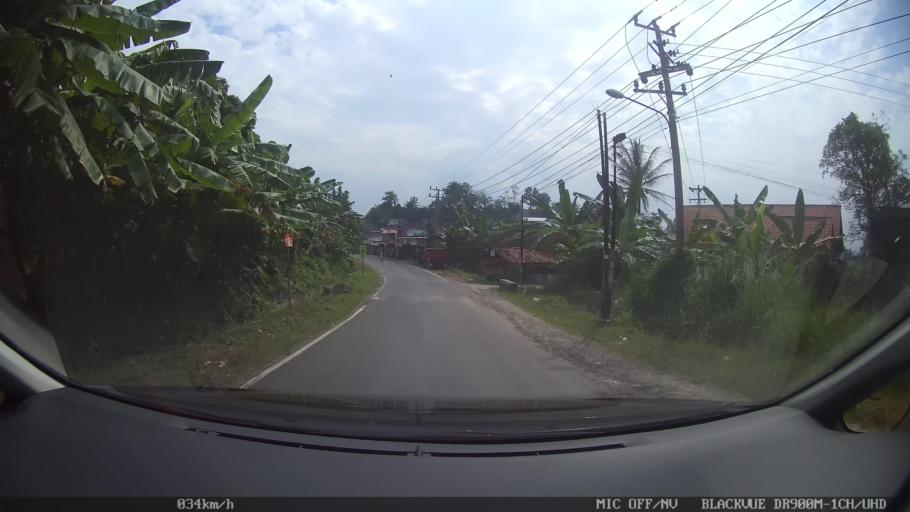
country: ID
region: Lampung
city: Bandarlampung
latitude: -5.4584
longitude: 105.2447
